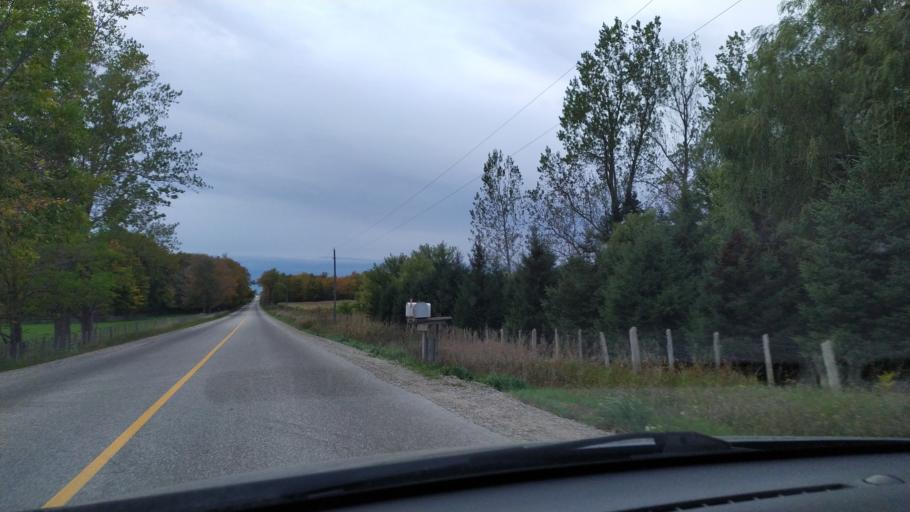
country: CA
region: Ontario
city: Waterloo
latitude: 43.5120
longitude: -80.7366
